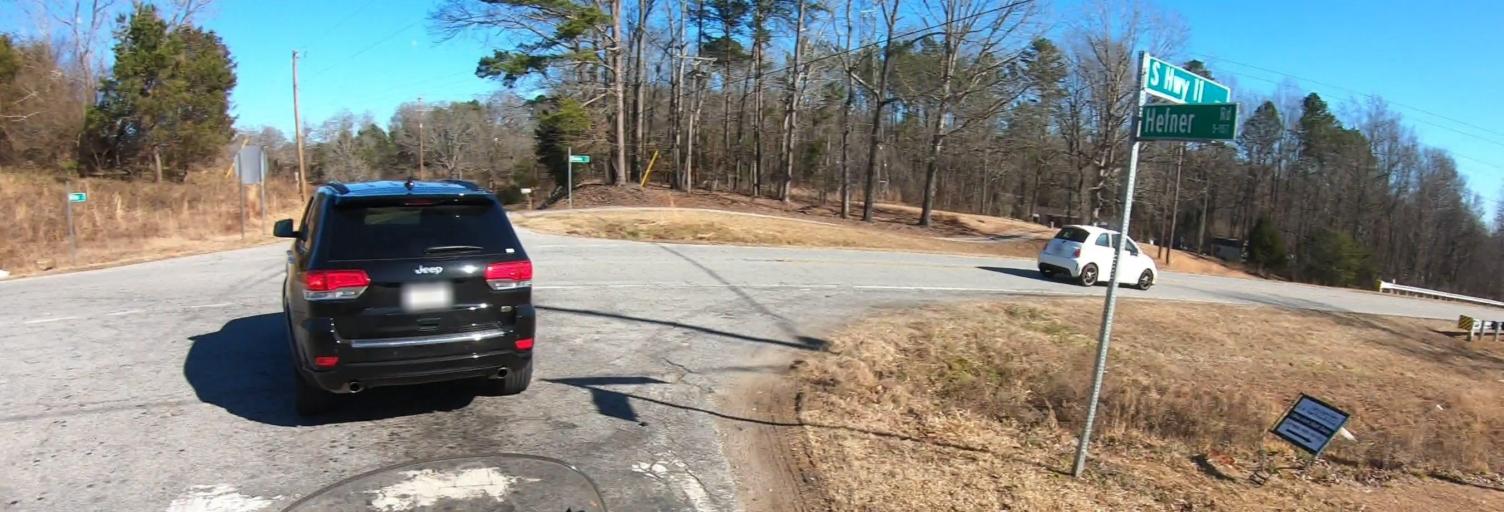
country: US
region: South Carolina
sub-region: Oconee County
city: Walhalla
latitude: 34.7270
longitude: -83.0603
